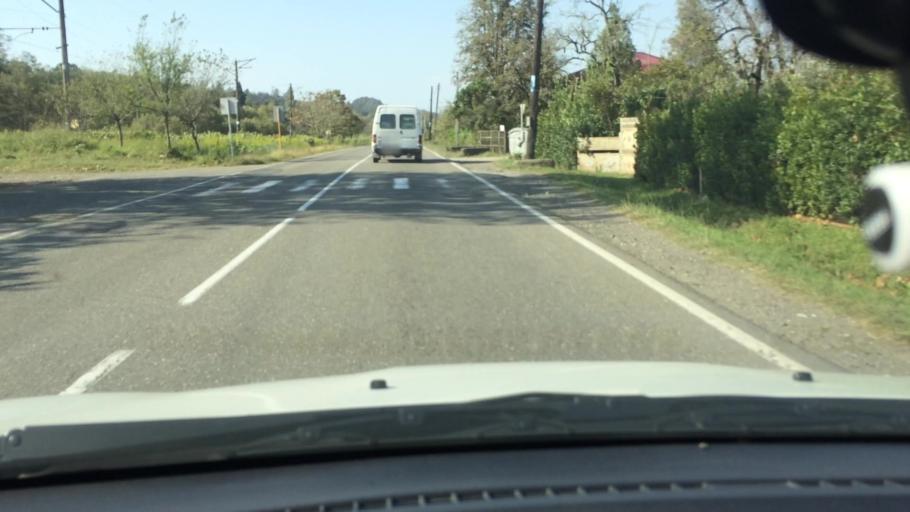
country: GE
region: Guria
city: Lanchkhuti
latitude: 42.0705
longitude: 41.8962
